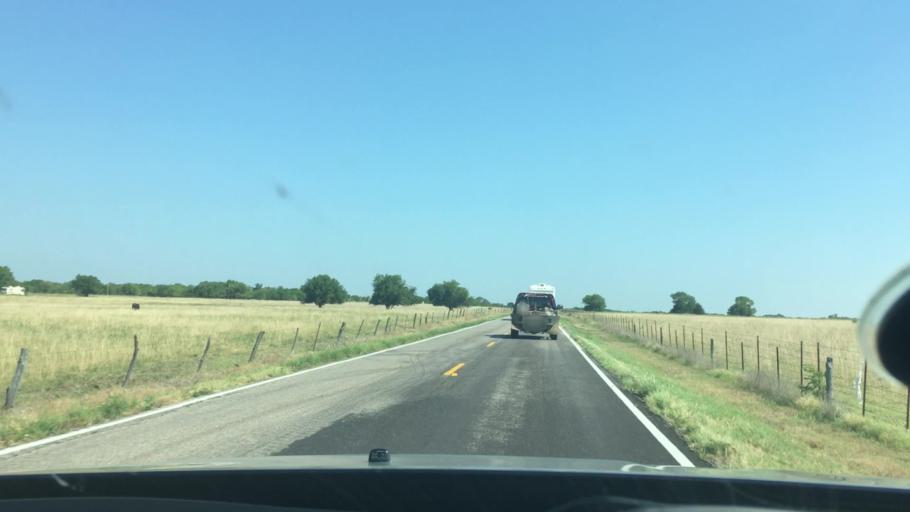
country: US
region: Oklahoma
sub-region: Johnston County
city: Tishomingo
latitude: 34.1768
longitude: -96.5112
